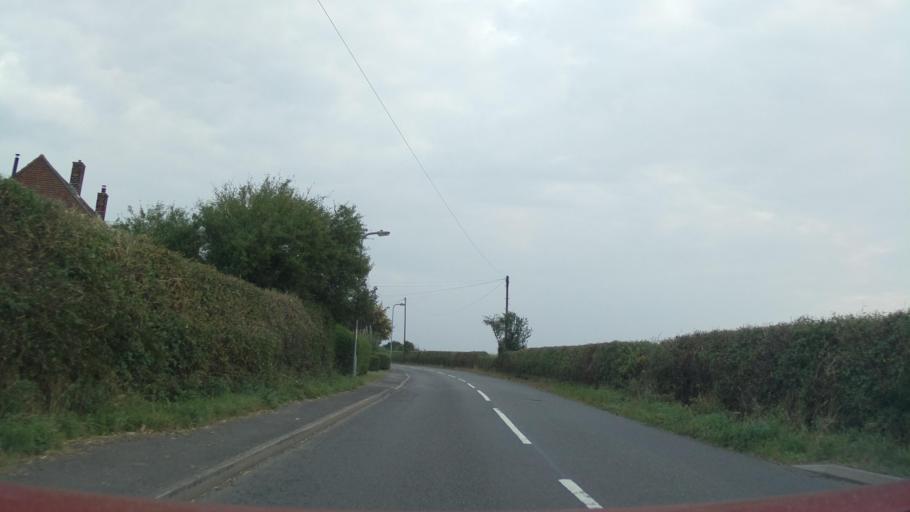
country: GB
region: England
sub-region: Lincolnshire
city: Skellingthorpe
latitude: 53.1406
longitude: -0.6458
